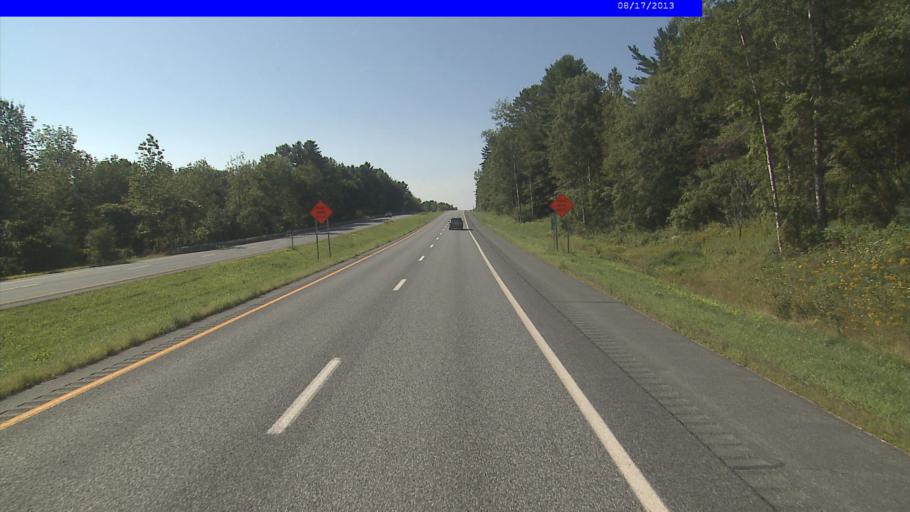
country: US
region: Vermont
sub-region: Windsor County
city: Windsor
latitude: 43.4813
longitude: -72.4068
